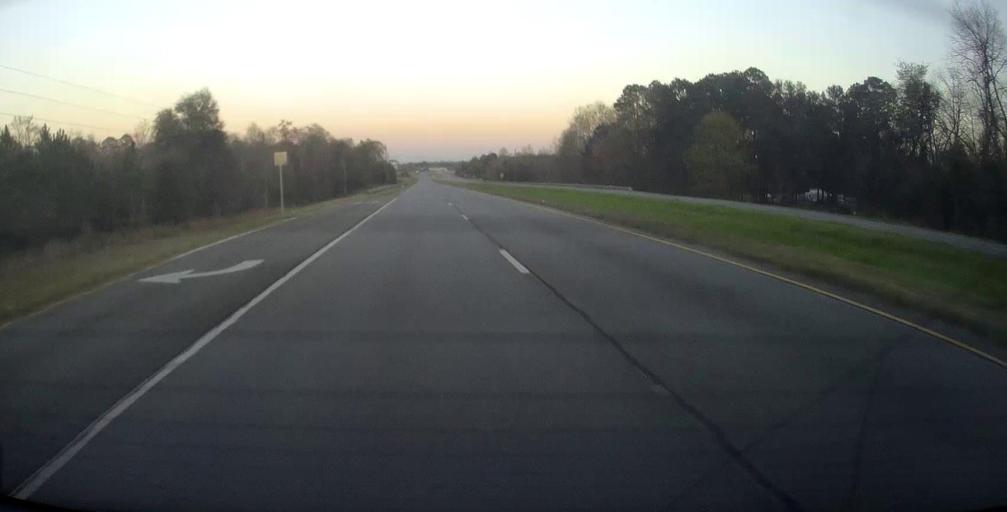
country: US
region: Georgia
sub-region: Dodge County
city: Eastman
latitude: 32.1767
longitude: -83.1731
